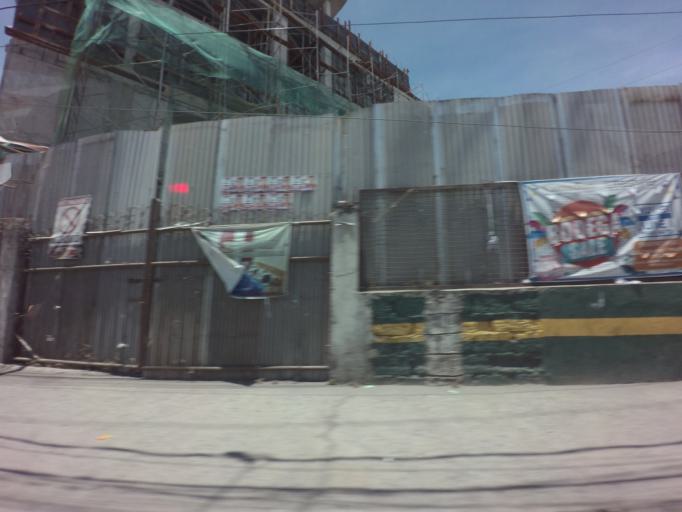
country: PH
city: Sambayanihan People's Village
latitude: 14.4927
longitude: 121.0148
